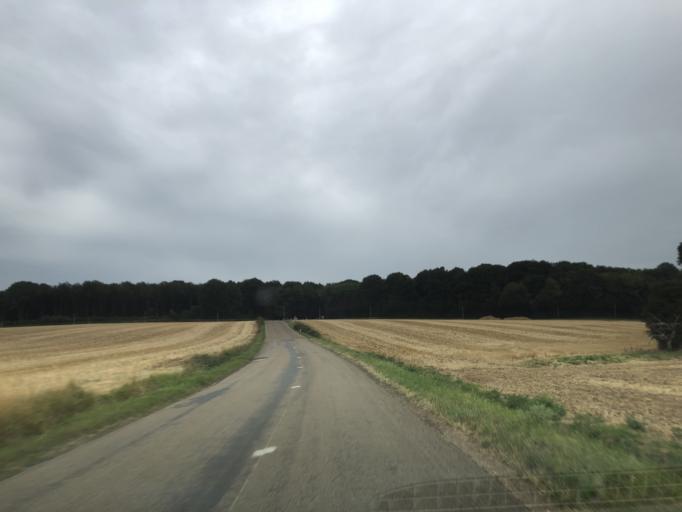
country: FR
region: Bourgogne
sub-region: Departement de l'Yonne
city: Charny
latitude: 47.9649
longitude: 3.1434
